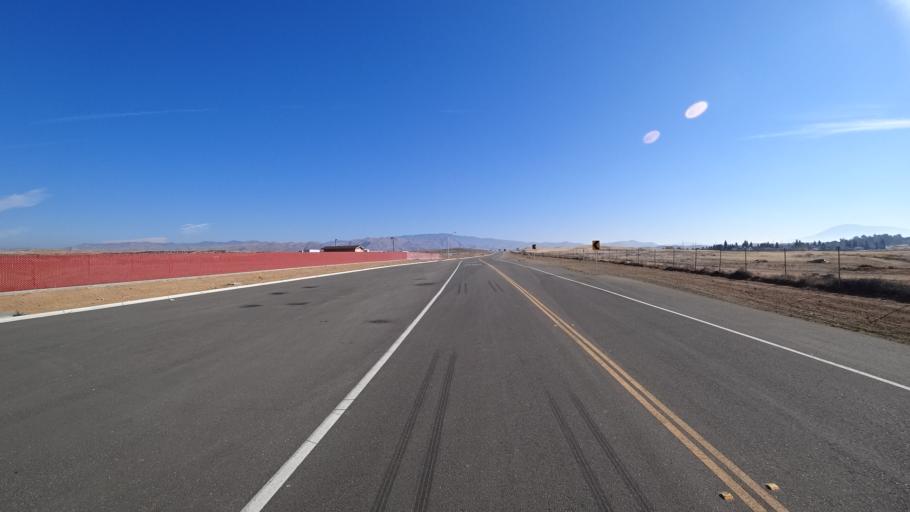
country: US
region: California
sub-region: Kern County
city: Oildale
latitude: 35.4126
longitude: -118.8782
